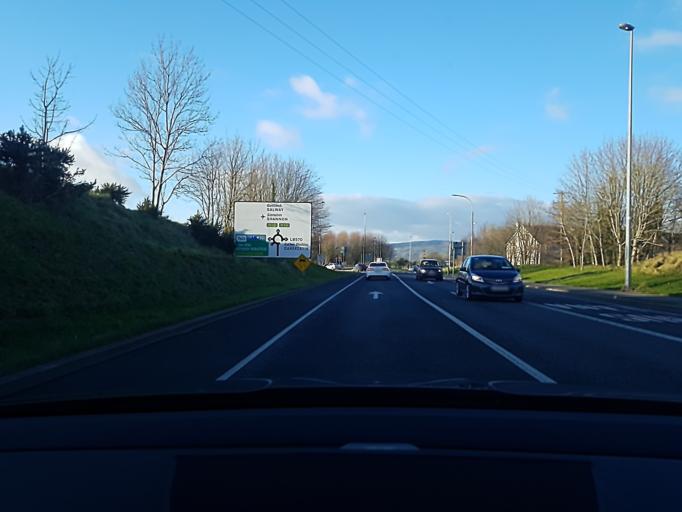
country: IE
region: Munster
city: Moyross
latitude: 52.6642
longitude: -8.6685
